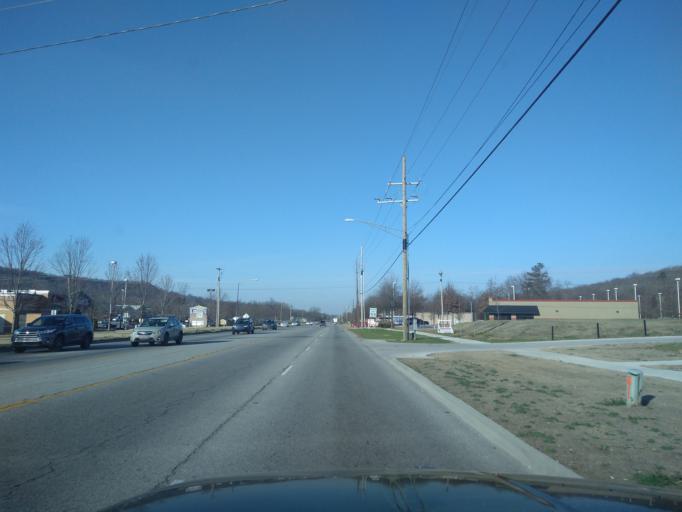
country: US
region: Arkansas
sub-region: Washington County
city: Farmington
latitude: 36.0515
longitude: -94.2040
